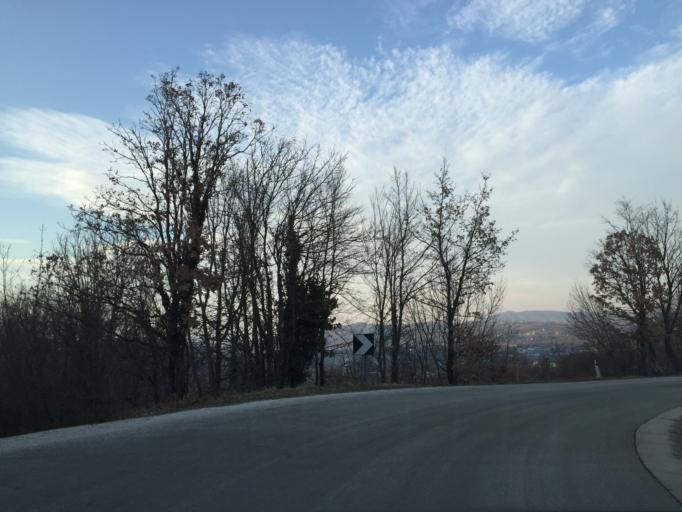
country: IT
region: Molise
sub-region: Provincia di Campobasso
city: Guardiaregia
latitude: 41.4460
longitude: 14.5501
